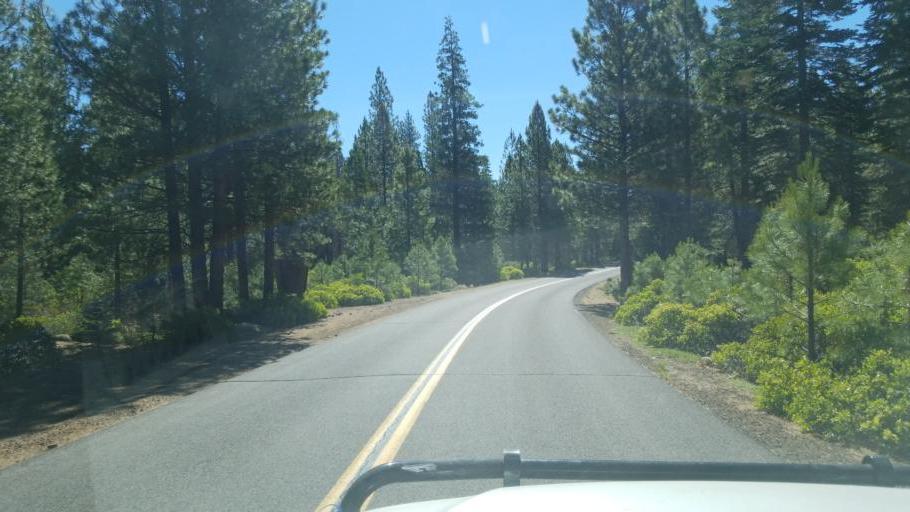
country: US
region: California
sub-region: Lassen County
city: Susanville
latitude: 40.5380
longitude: -120.7861
